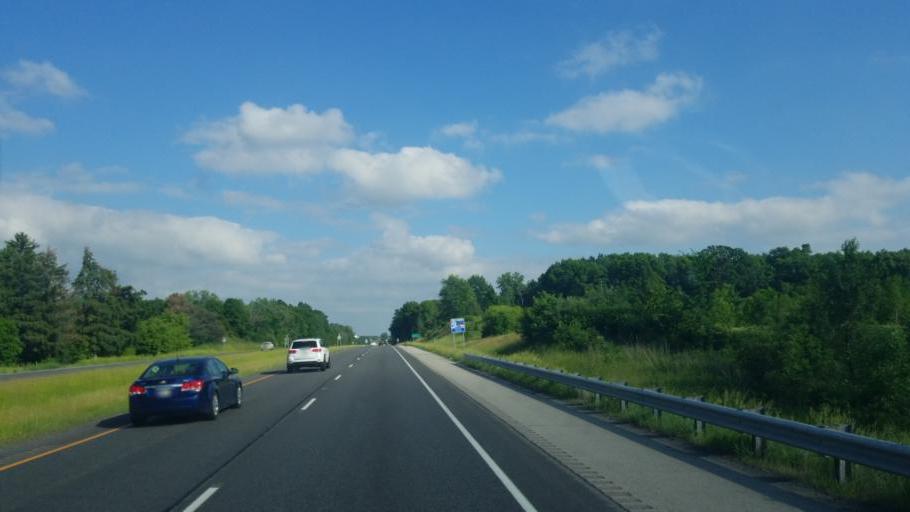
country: US
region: Indiana
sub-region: Whitley County
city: Columbia City
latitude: 41.1596
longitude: -85.4630
